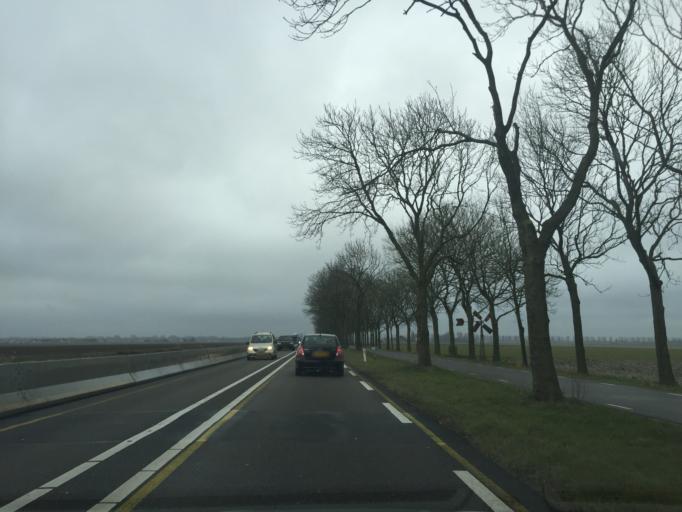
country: NL
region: South Holland
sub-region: Gemeente Kaag en Braassem
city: Leimuiden
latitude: 52.1823
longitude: 4.6720
